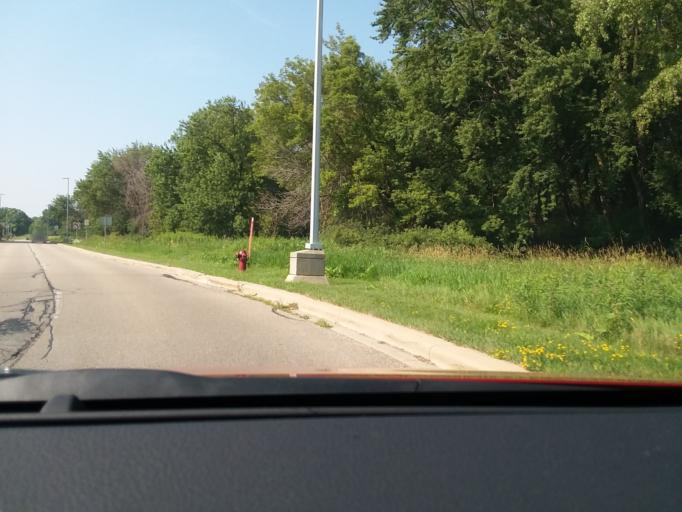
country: US
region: Wisconsin
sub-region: Dane County
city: Maple Bluff
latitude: 43.1385
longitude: -89.3479
